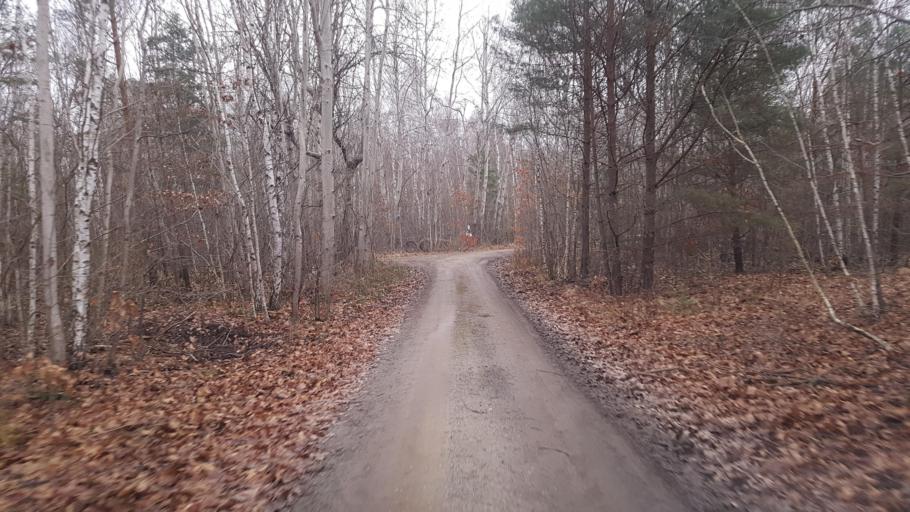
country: DE
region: Brandenburg
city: Plessa
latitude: 51.4976
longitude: 13.6401
